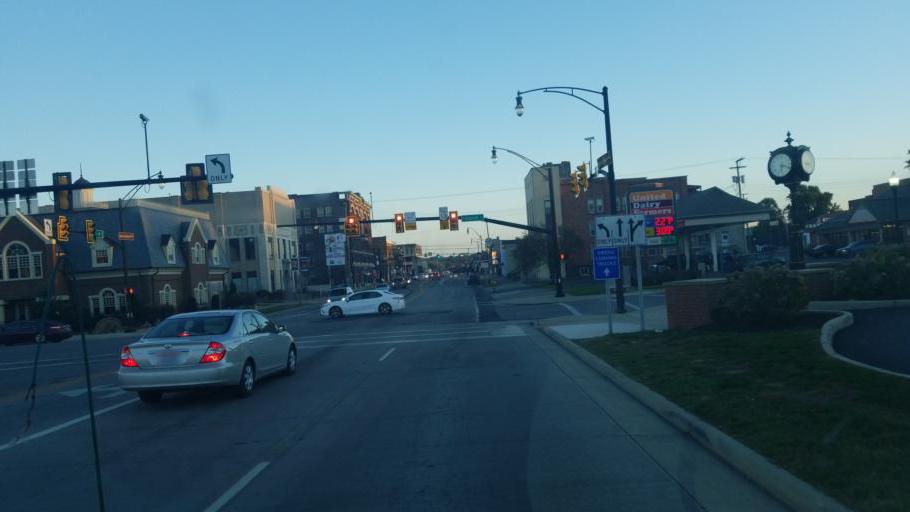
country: US
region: Ohio
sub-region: Licking County
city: Newark
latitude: 40.0602
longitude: -82.4058
